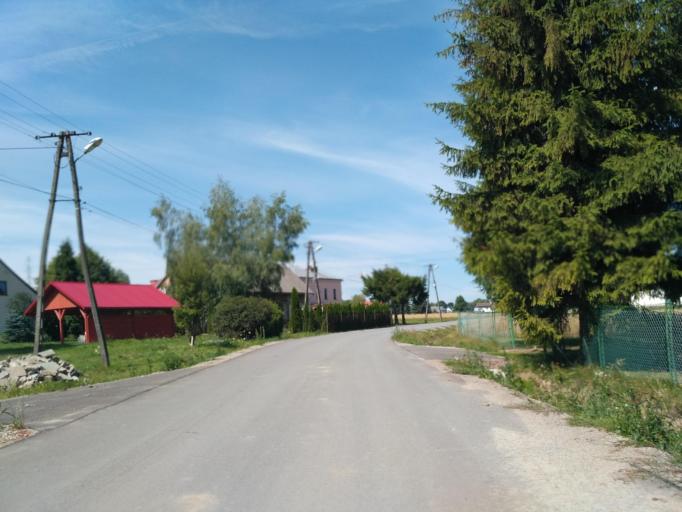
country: PL
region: Subcarpathian Voivodeship
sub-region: Powiat brzozowski
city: Jablonica Polska
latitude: 49.6927
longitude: 21.8742
